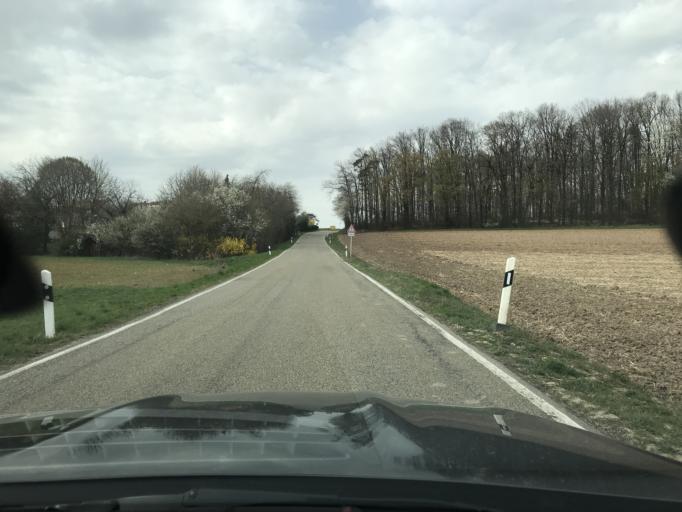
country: DE
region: Baden-Wuerttemberg
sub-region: Regierungsbezirk Stuttgart
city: Burgstetten
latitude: 48.9178
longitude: 9.3775
